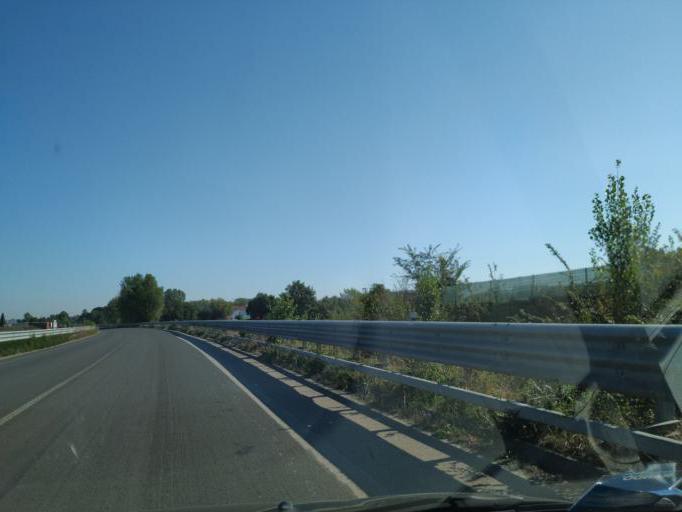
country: IT
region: Emilia-Romagna
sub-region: Provincia di Bologna
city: San Giovanni in Persiceto
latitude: 44.6467
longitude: 11.1732
